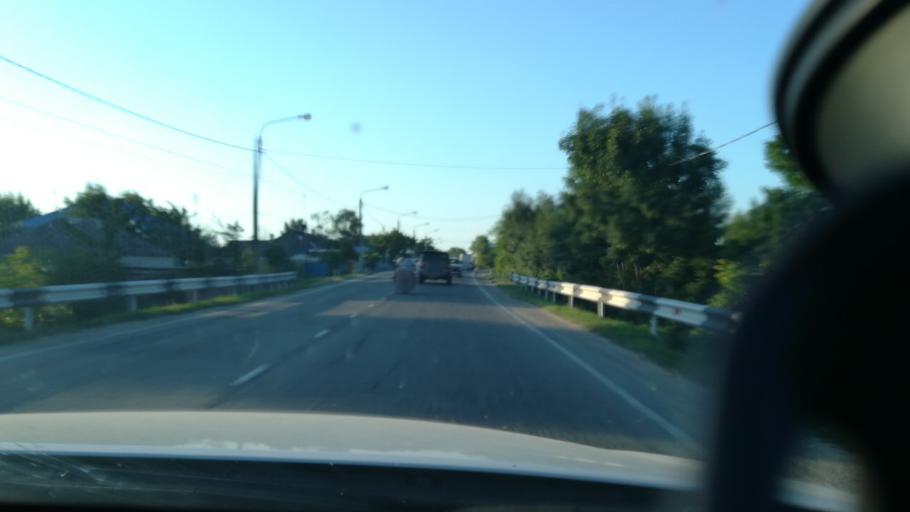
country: RU
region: Krasnodarskiy
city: Gostagayevskaya
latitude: 45.0191
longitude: 37.5024
